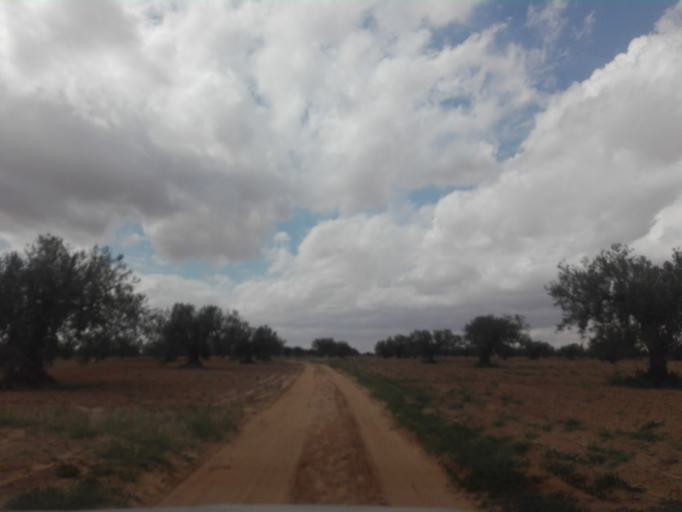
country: TN
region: Safaqis
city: Sfax
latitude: 34.6919
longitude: 10.4502
